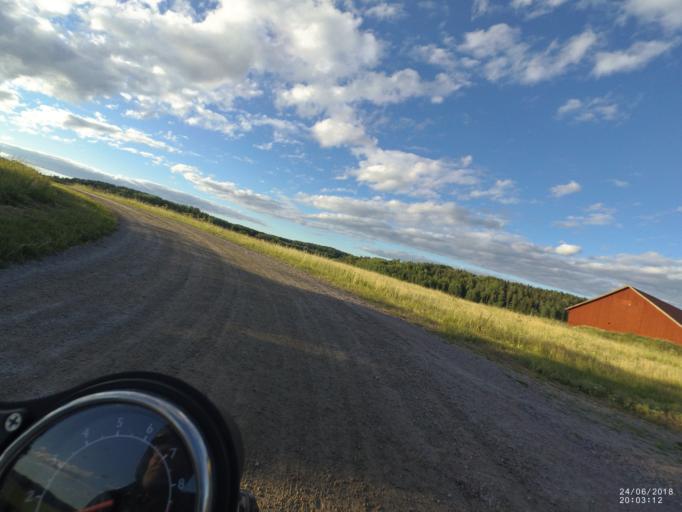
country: SE
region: Soedermanland
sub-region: Nykopings Kommun
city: Nykoping
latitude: 58.7968
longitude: 17.1237
